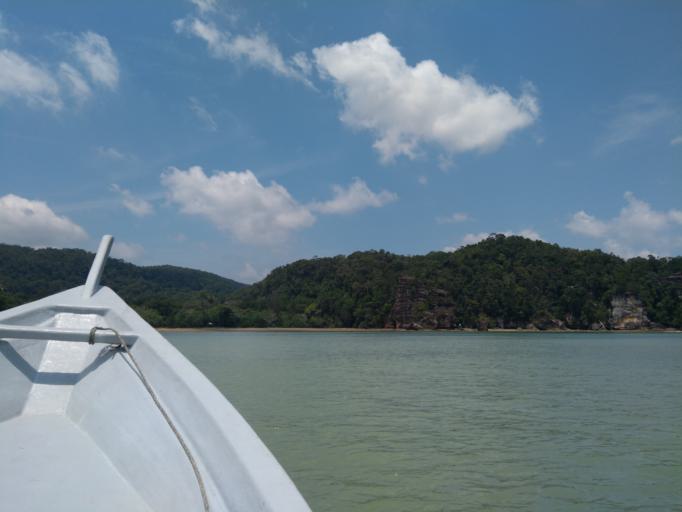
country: MY
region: Sarawak
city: Kuching
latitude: 1.7197
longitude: 110.4422
